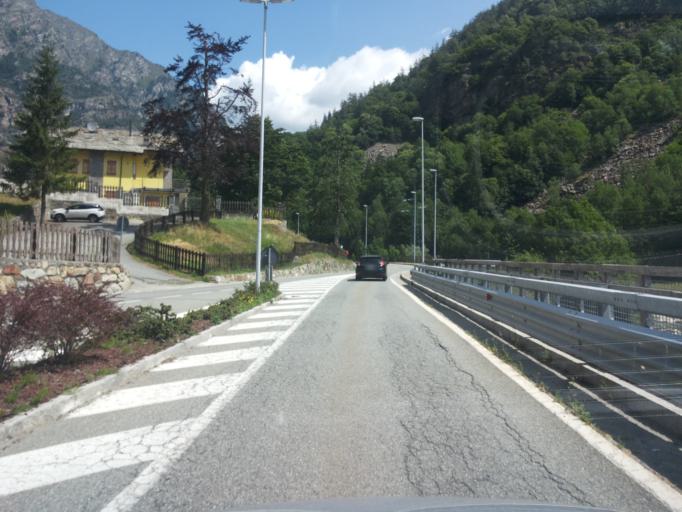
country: IT
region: Aosta Valley
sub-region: Valle d'Aosta
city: Issime
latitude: 45.6805
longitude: 7.8567
